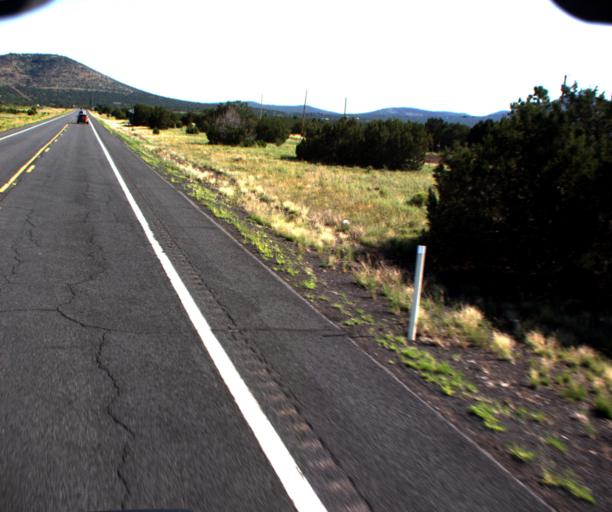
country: US
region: Arizona
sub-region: Coconino County
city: Williams
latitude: 35.3704
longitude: -112.1639
